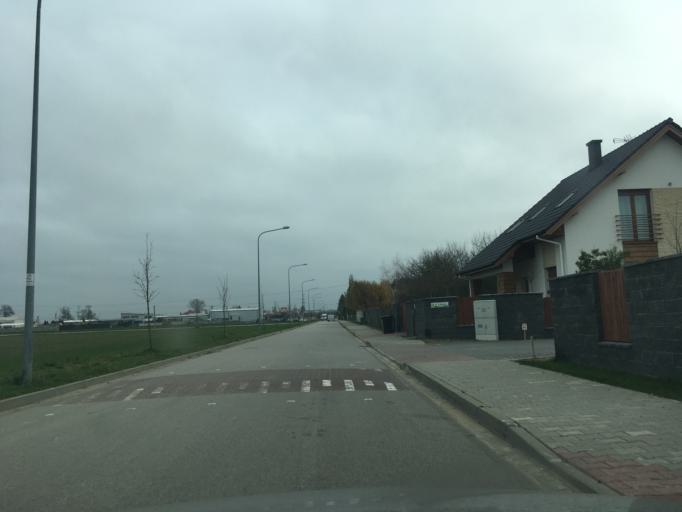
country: PL
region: Masovian Voivodeship
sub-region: Powiat piaseczynski
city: Lesznowola
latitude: 52.0828
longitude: 20.9536
